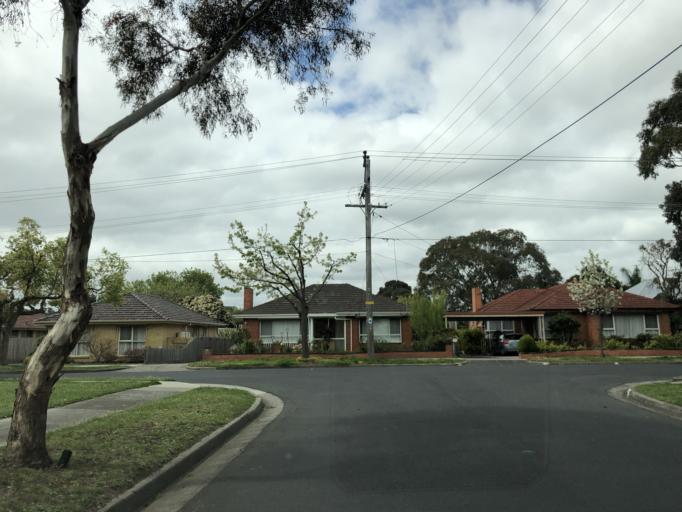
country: AU
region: Victoria
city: Burwood East
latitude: -37.8464
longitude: 145.1486
